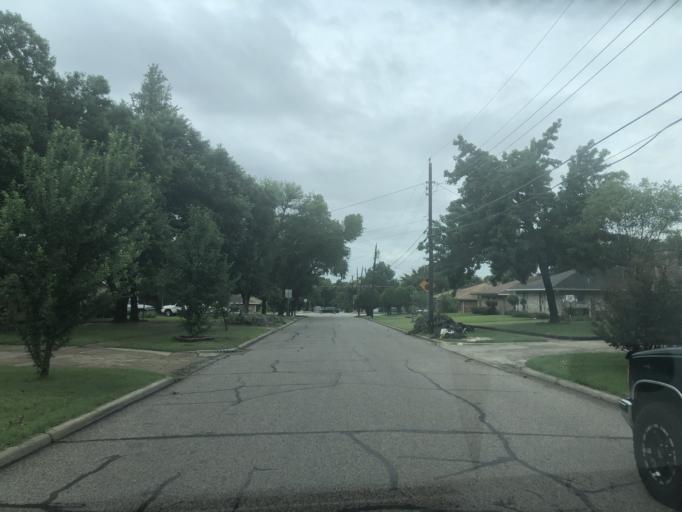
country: US
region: Texas
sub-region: Dallas County
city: Irving
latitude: 32.8022
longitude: -96.9418
